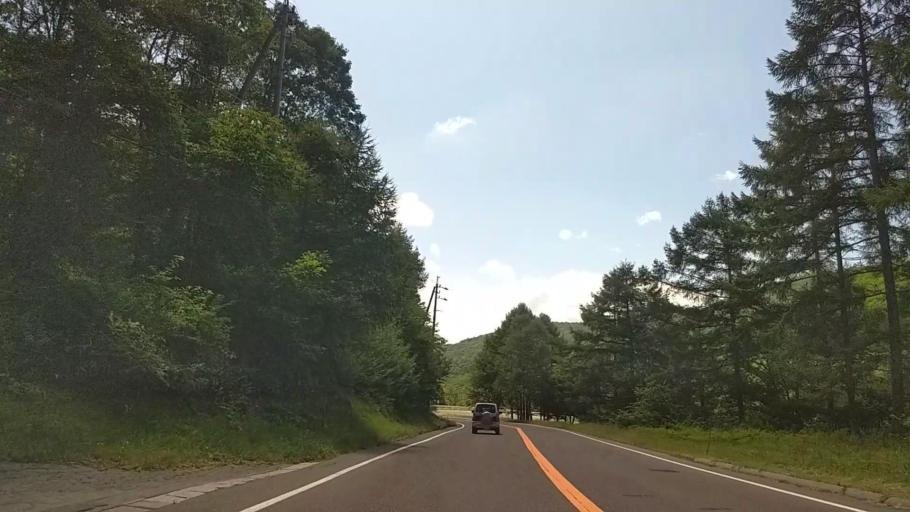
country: JP
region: Nagano
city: Chino
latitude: 36.0842
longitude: 138.2231
